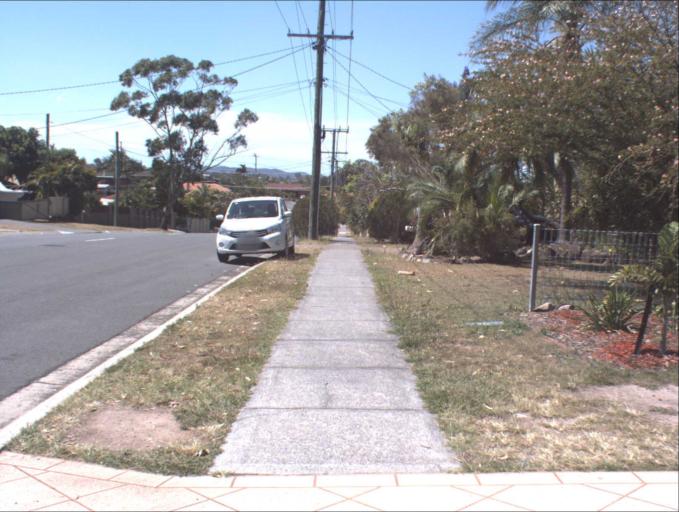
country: AU
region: Queensland
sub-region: Logan
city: Windaroo
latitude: -27.7271
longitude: 153.2028
